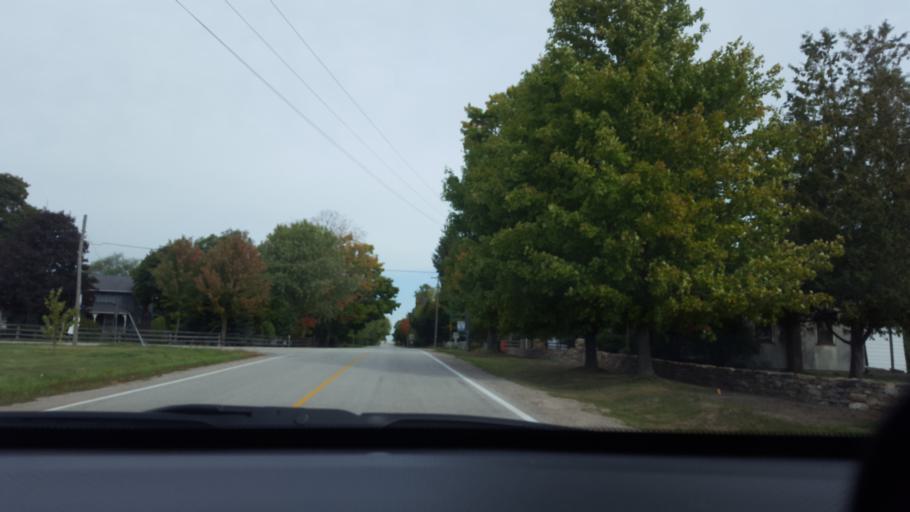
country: CA
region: Ontario
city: Newmarket
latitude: 44.0118
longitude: -79.5500
